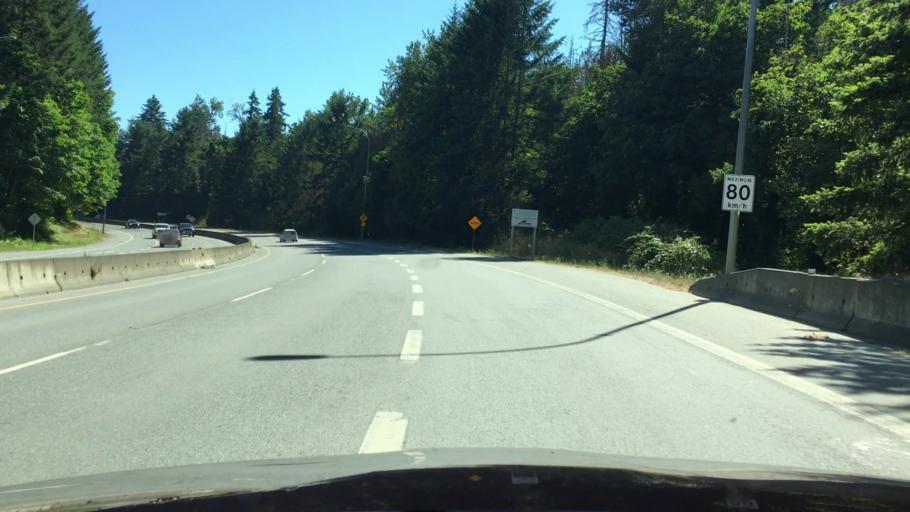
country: CA
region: British Columbia
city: North Saanich
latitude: 48.6757
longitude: -123.4279
